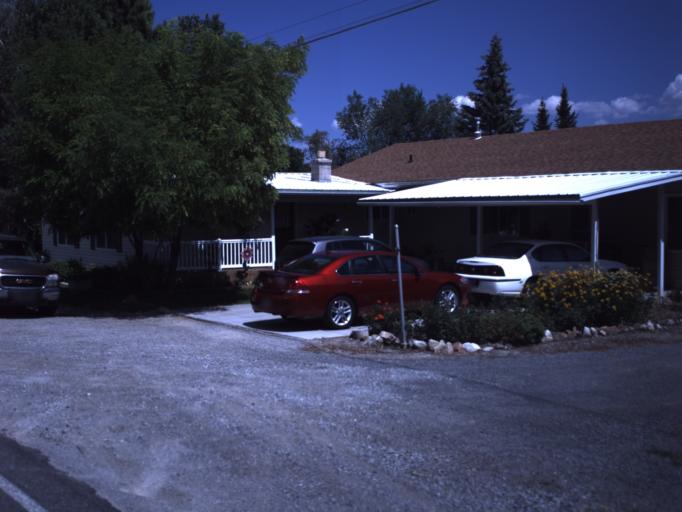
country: US
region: Idaho
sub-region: Bear Lake County
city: Paris
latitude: 41.9253
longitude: -111.3971
